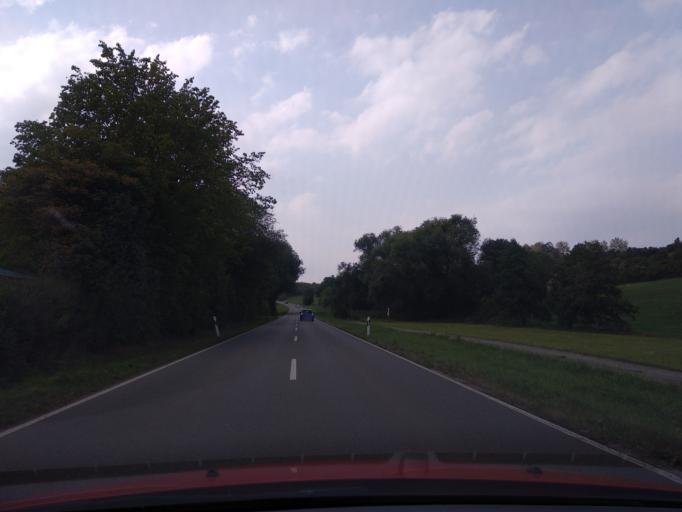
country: DE
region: Hesse
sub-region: Regierungsbezirk Kassel
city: Calden
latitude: 51.3750
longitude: 9.3826
